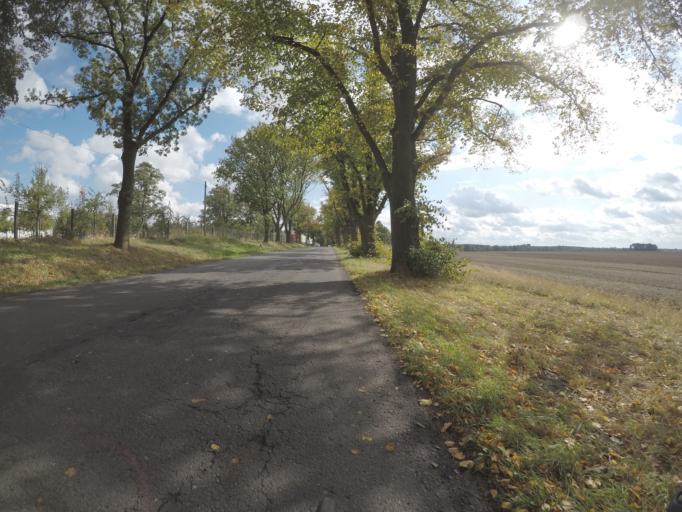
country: DE
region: Brandenburg
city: Werftpfuhl
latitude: 52.6047
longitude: 13.8075
